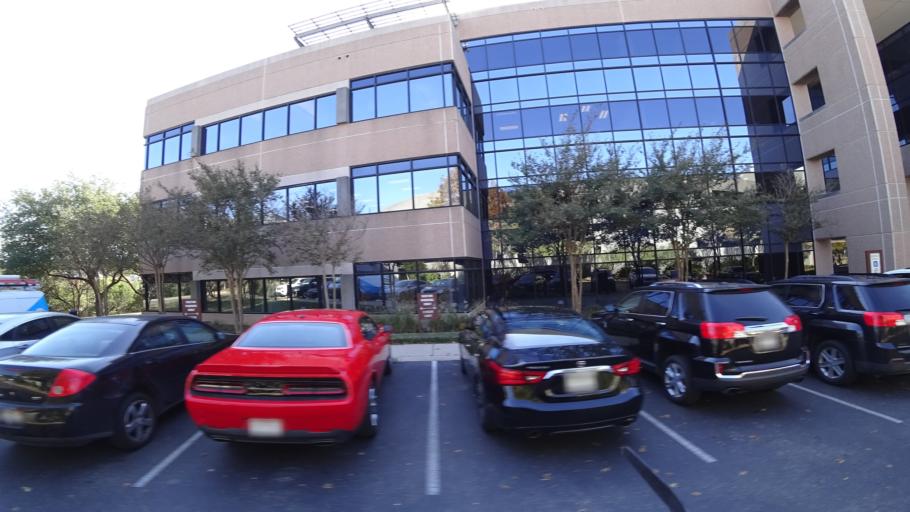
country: US
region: Texas
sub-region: Williamson County
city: Anderson Mill
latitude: 30.3920
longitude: -97.8503
